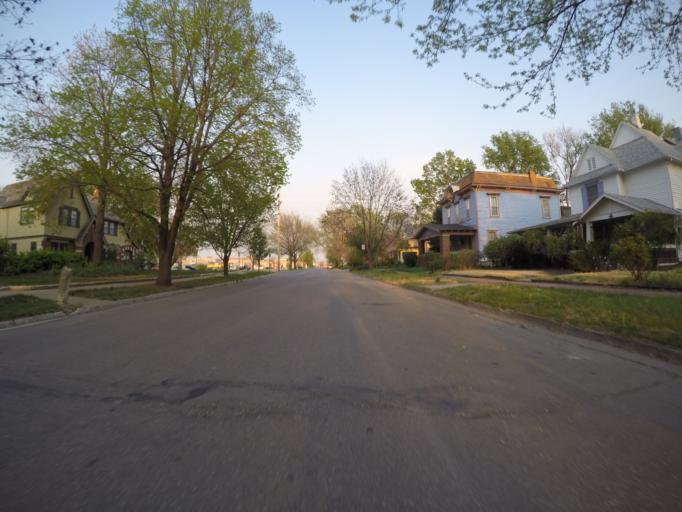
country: US
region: Kansas
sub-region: Riley County
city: Manhattan
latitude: 39.1783
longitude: -96.5657
